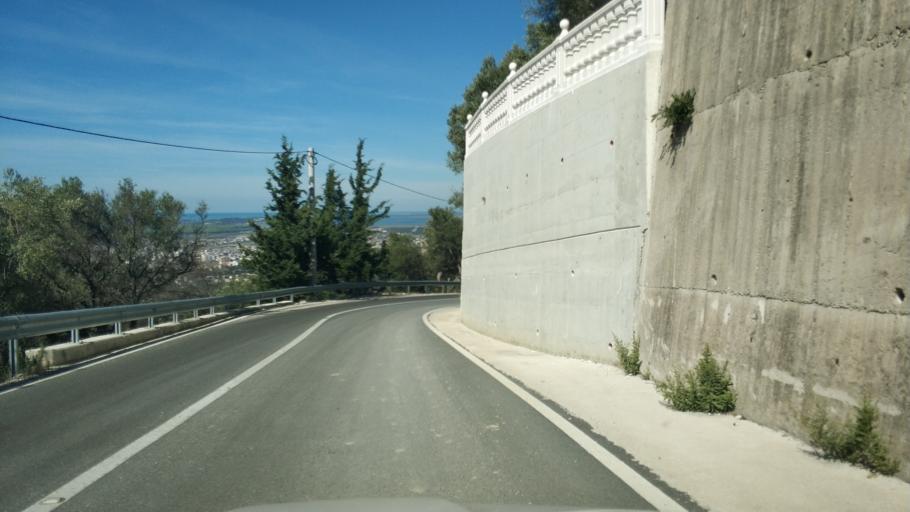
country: AL
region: Vlore
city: Vlore
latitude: 40.4507
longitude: 19.5160
